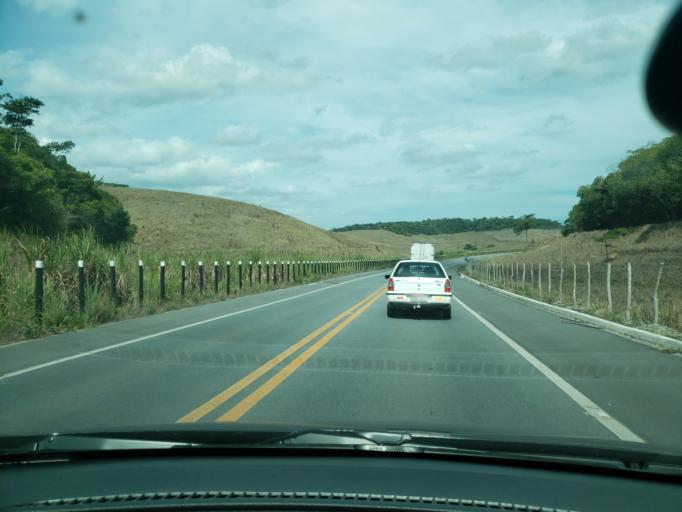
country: BR
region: Alagoas
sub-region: Murici
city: Murici
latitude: -9.3303
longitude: -35.9072
